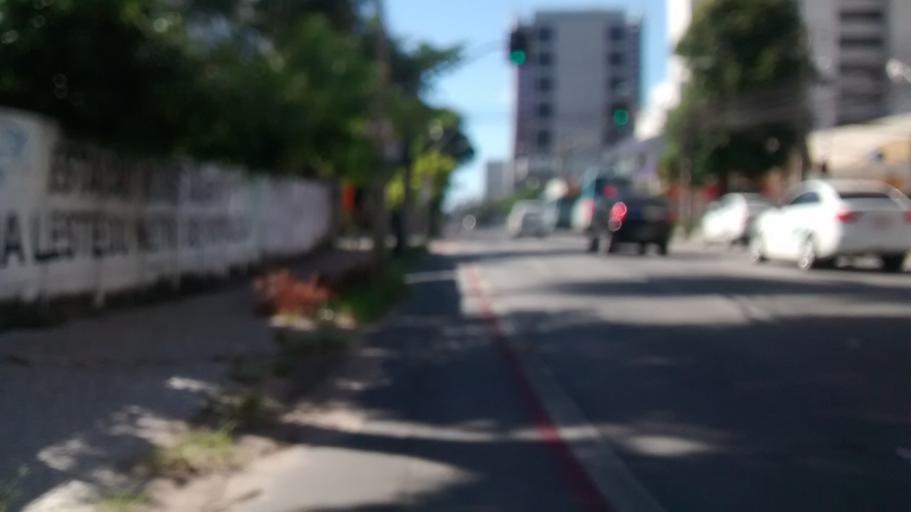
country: BR
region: Ceara
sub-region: Fortaleza
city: Fortaleza
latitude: -3.7348
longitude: -38.5026
